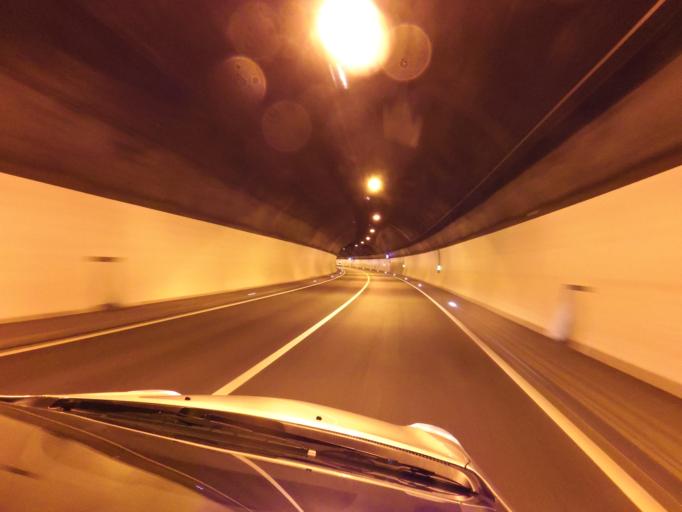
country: DE
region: Rheinland-Pfalz
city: Annweiler am Trifels
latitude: 49.2088
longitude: 7.9685
